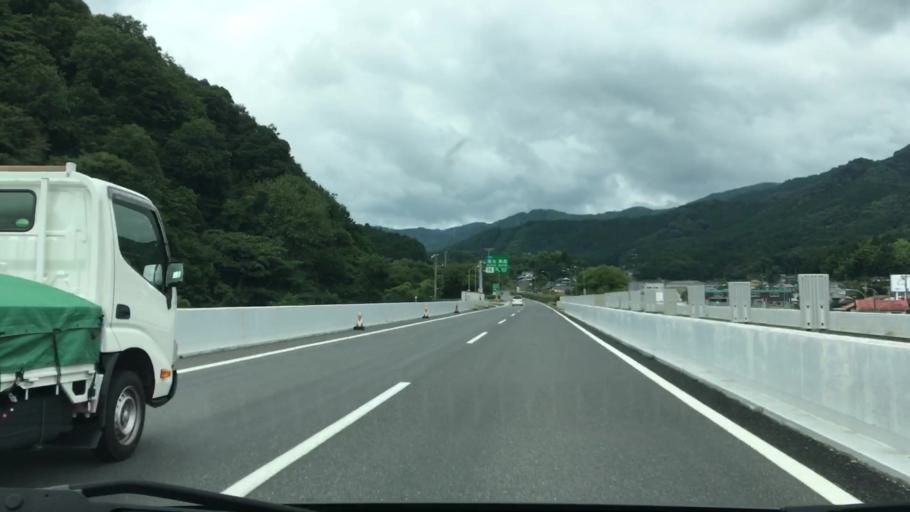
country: JP
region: Okayama
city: Tsuyama
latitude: 35.0246
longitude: 133.7516
